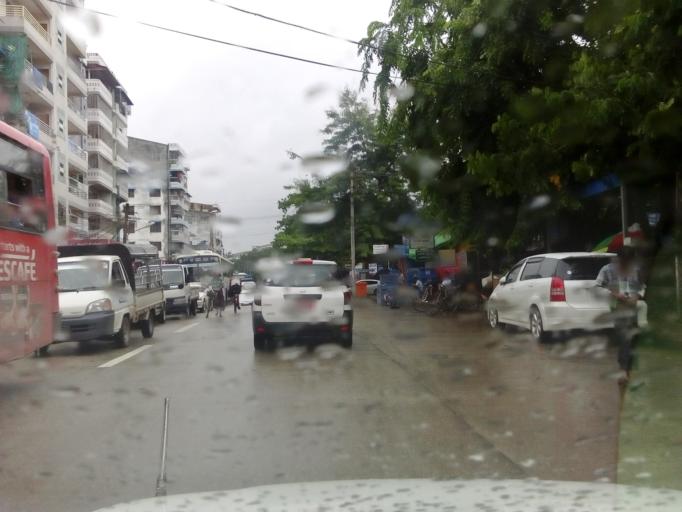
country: MM
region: Yangon
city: Yangon
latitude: 16.8133
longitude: 96.1748
